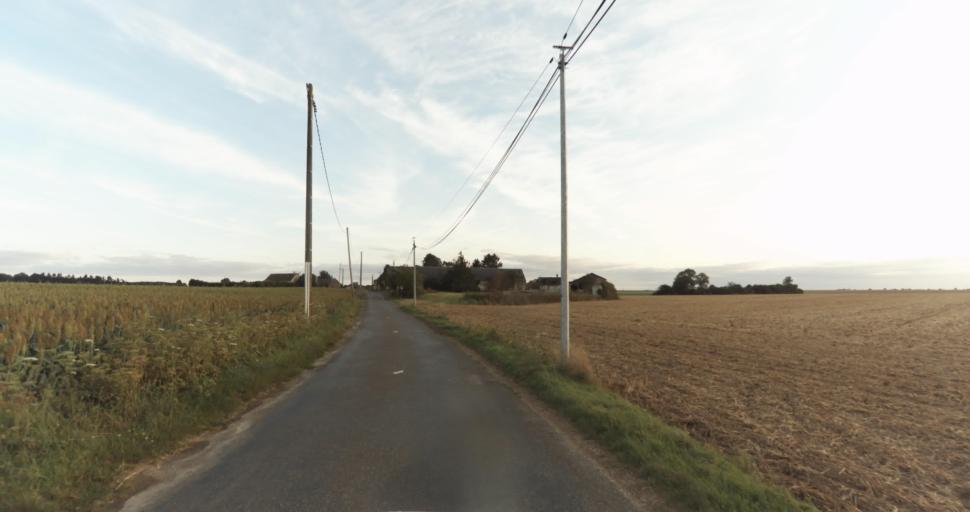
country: FR
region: Haute-Normandie
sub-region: Departement de l'Eure
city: La Madeleine-de-Nonancourt
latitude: 48.8891
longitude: 1.2362
